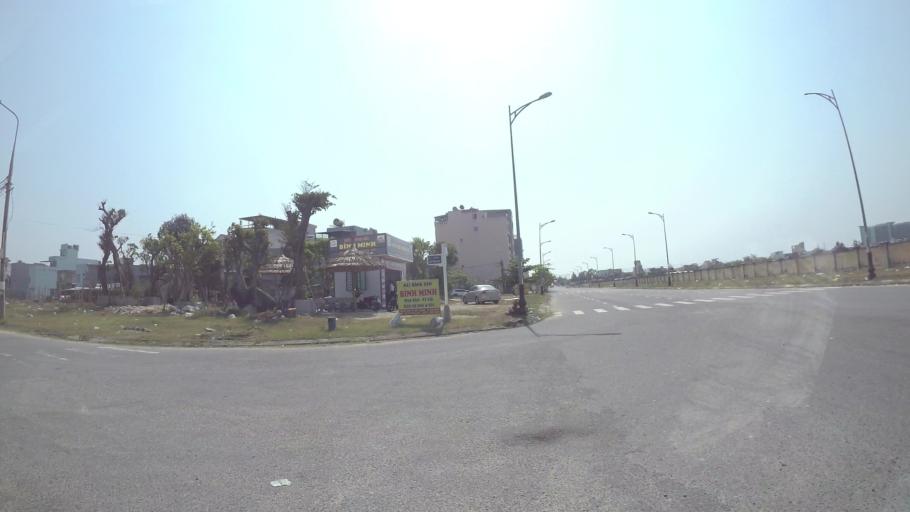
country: VN
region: Da Nang
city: Ngu Hanh Son
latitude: 16.0207
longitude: 108.2562
